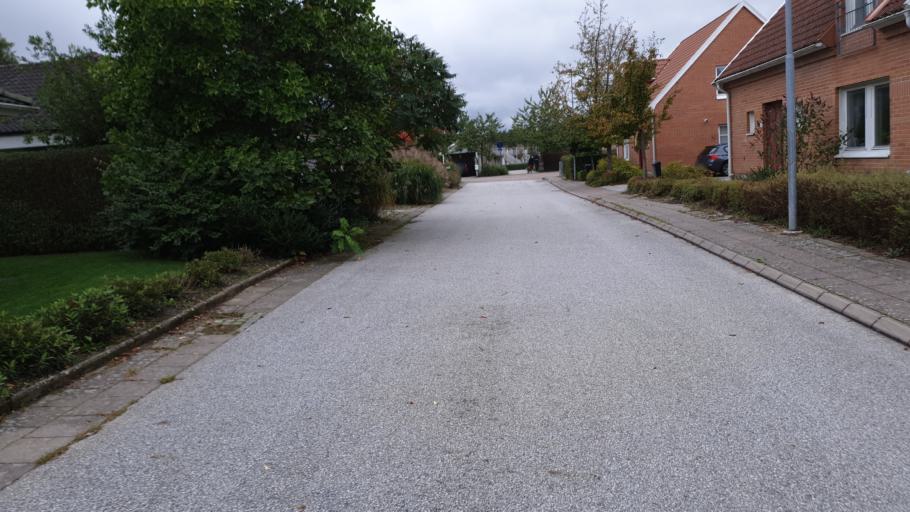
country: SE
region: Skane
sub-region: Lunds Kommun
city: Lund
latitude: 55.7153
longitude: 13.2404
